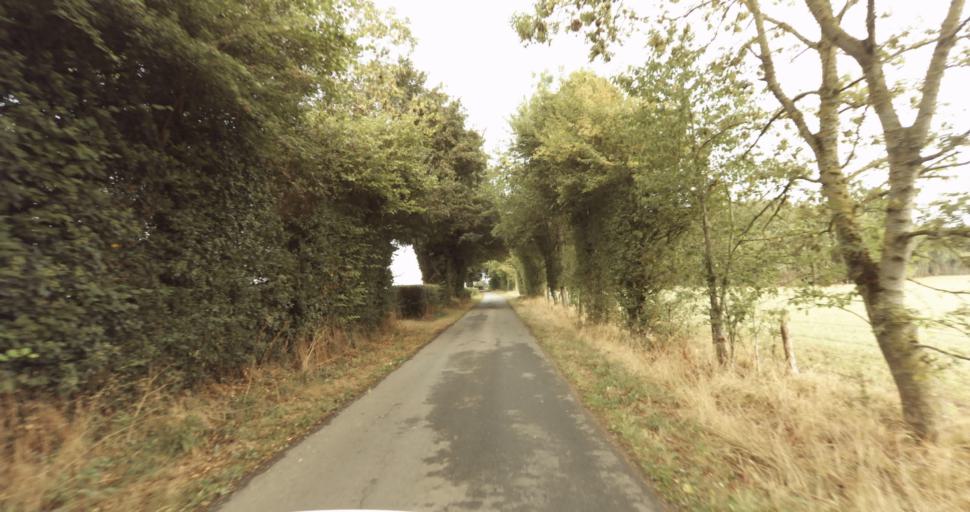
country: FR
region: Lower Normandy
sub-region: Departement de l'Orne
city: Vimoutiers
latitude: 48.9314
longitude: 0.1474
